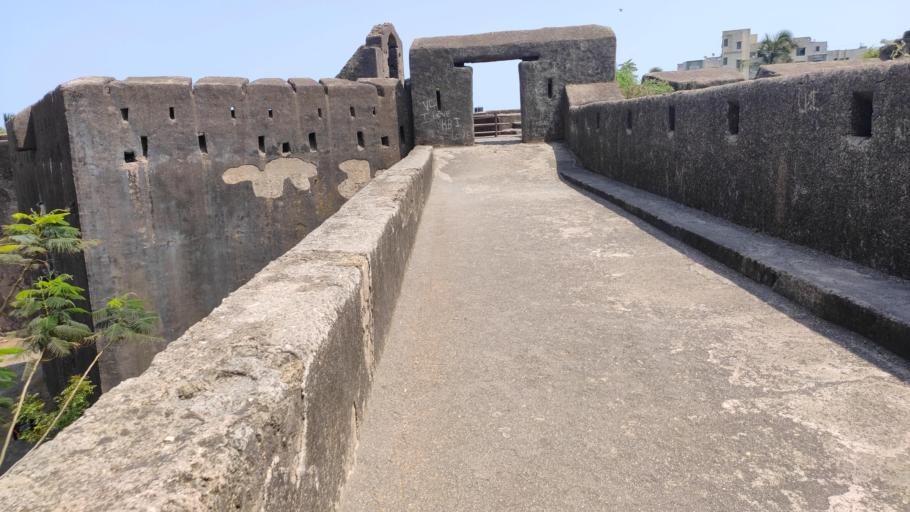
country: IN
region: Daman and Diu
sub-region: Daman District
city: Daman
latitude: 20.4137
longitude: 72.8325
